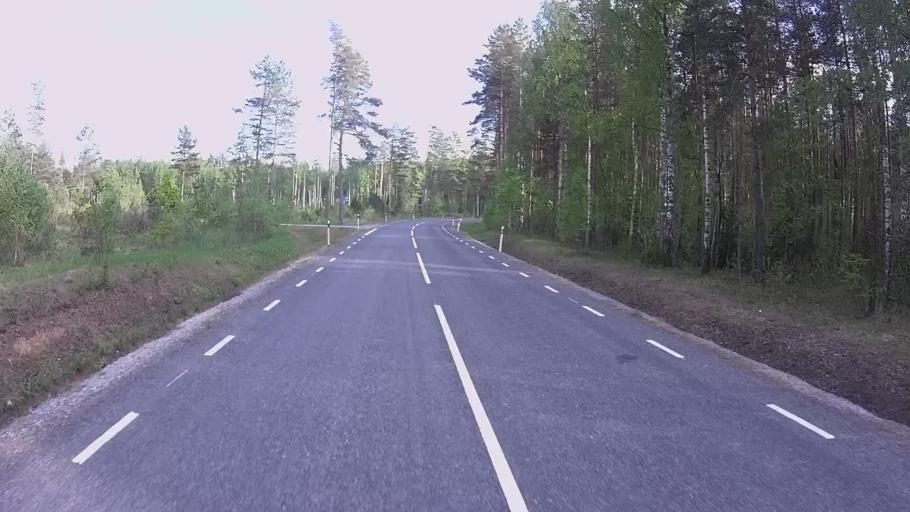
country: EE
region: Jogevamaa
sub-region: Mustvee linn
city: Mustvee
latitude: 59.0003
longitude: 27.1507
